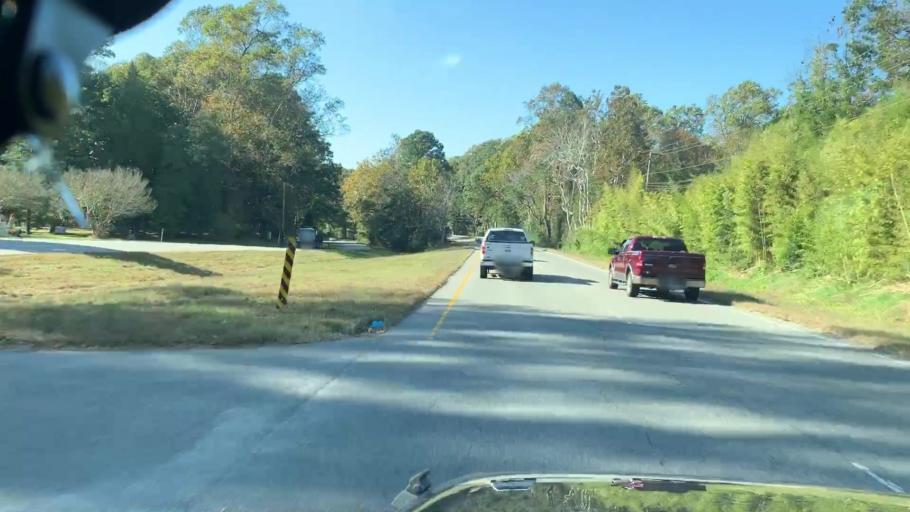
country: US
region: Virginia
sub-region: James City County
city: Williamsburg
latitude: 37.3760
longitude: -76.7850
